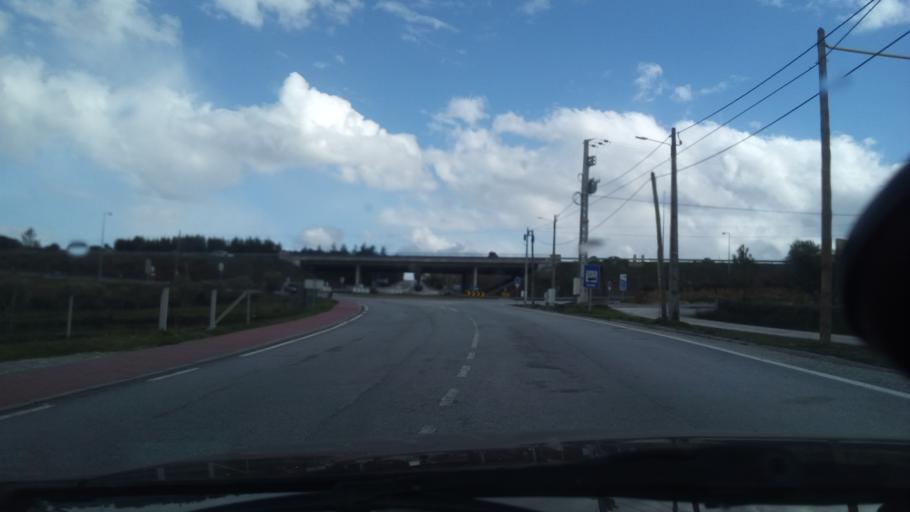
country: PT
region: Guarda
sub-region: Celorico da Beira
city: Celorico da Beira
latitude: 40.6369
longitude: -7.3526
